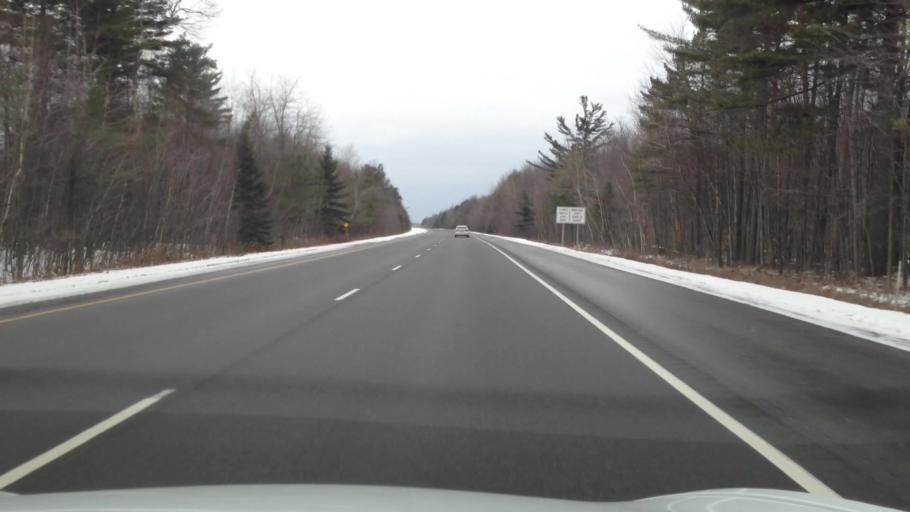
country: CA
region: Quebec
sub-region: Laurentides
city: Brownsburg-Chatham
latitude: 45.5576
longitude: -74.4637
